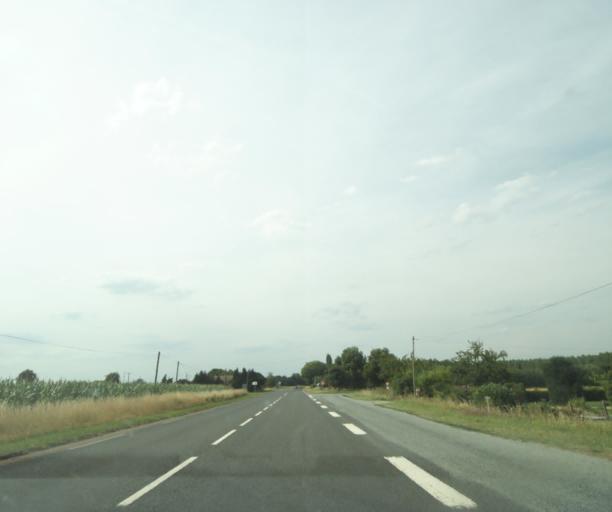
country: FR
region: Pays de la Loire
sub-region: Departement de la Sarthe
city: Ecommoy
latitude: 47.8515
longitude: 0.2542
